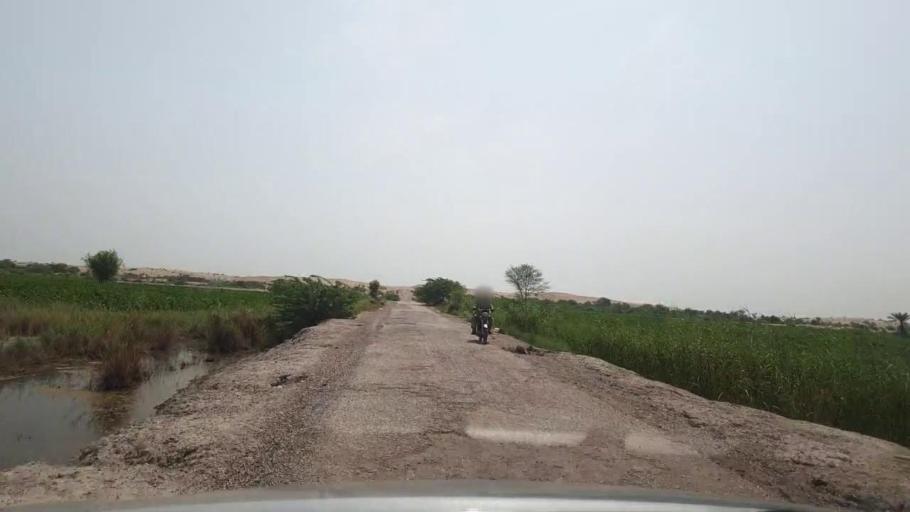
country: PK
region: Sindh
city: Rohri
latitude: 27.6181
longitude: 69.1105
